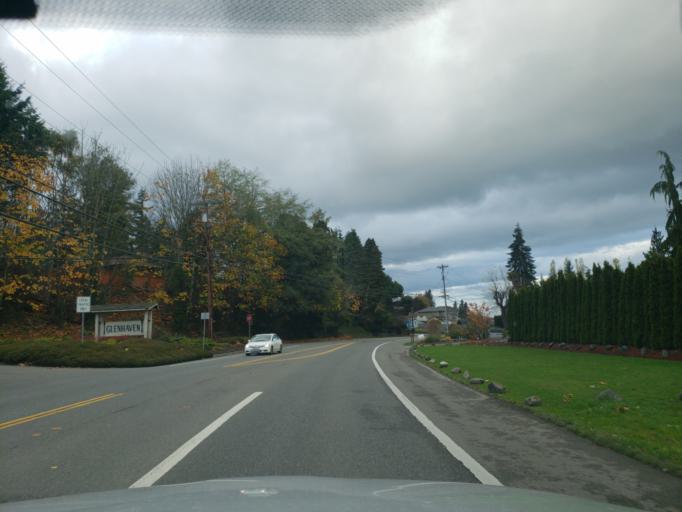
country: US
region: Washington
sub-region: Snohomish County
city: Everett
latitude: 47.9574
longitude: -122.2403
